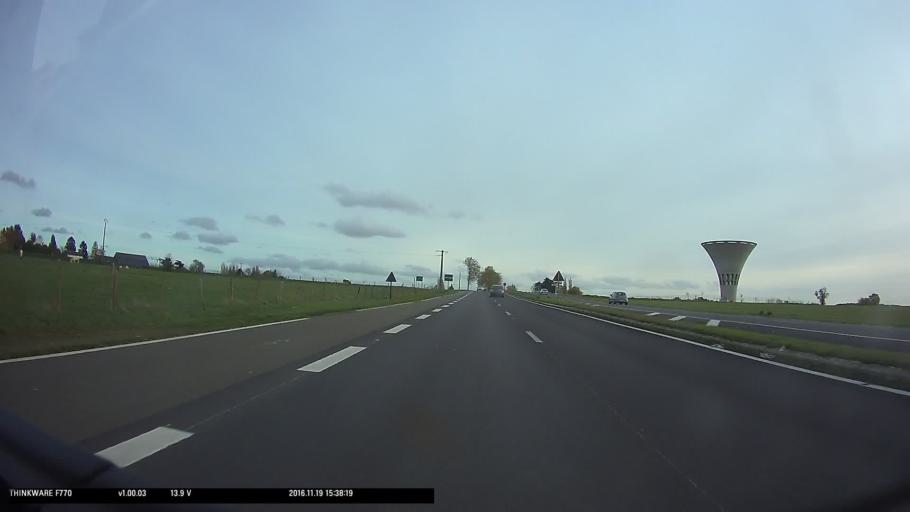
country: FR
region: Ile-de-France
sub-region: Departement du Val-d'Oise
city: Osny
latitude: 49.0860
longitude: 2.0640
